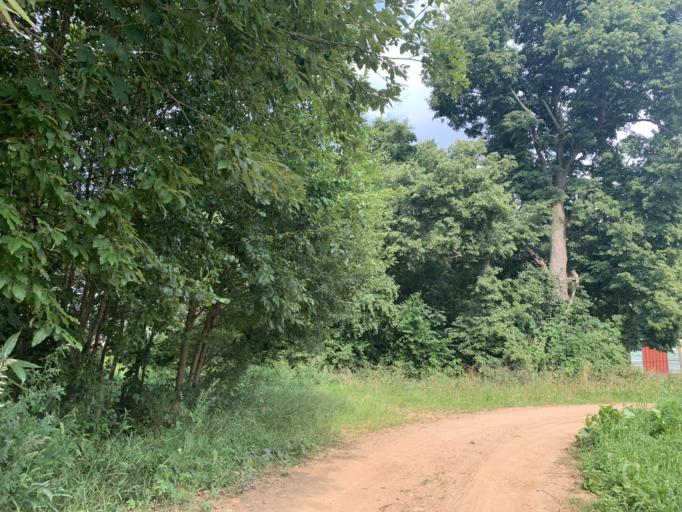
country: BY
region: Minsk
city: Nyasvizh
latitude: 53.1958
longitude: 26.6660
